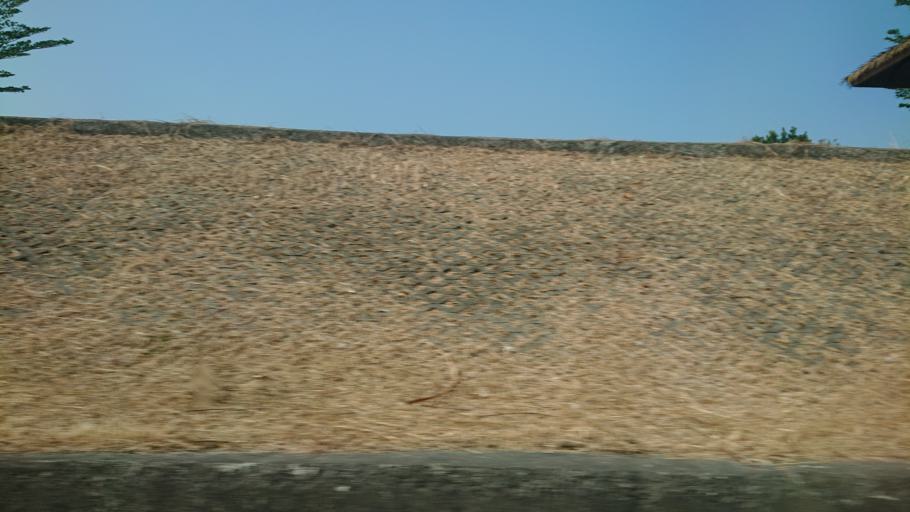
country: TW
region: Taiwan
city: Lugu
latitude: 23.7553
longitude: 120.6590
